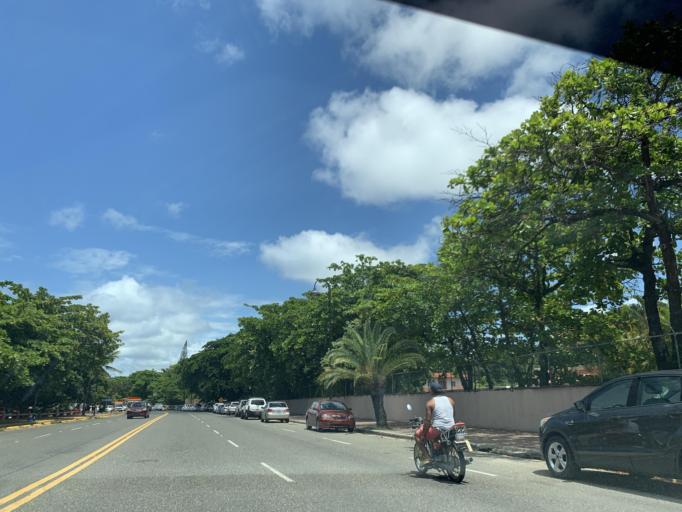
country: DO
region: Puerto Plata
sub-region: Puerto Plata
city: Puerto Plata
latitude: 19.7911
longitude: -70.6733
